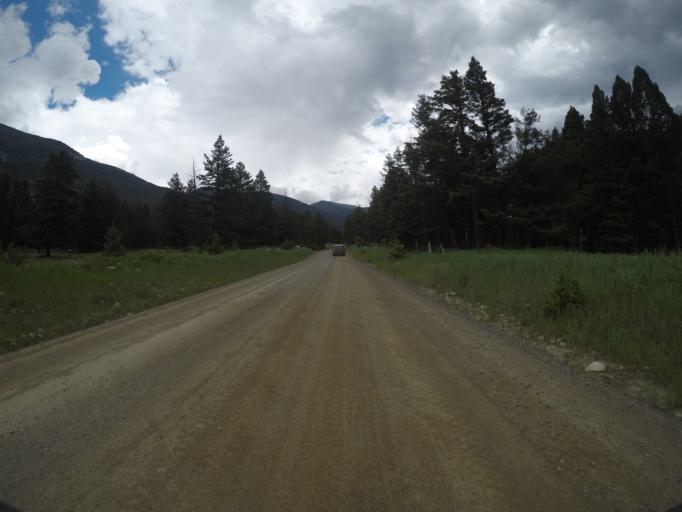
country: US
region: Montana
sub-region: Park County
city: Livingston
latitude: 45.4802
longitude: -110.2102
